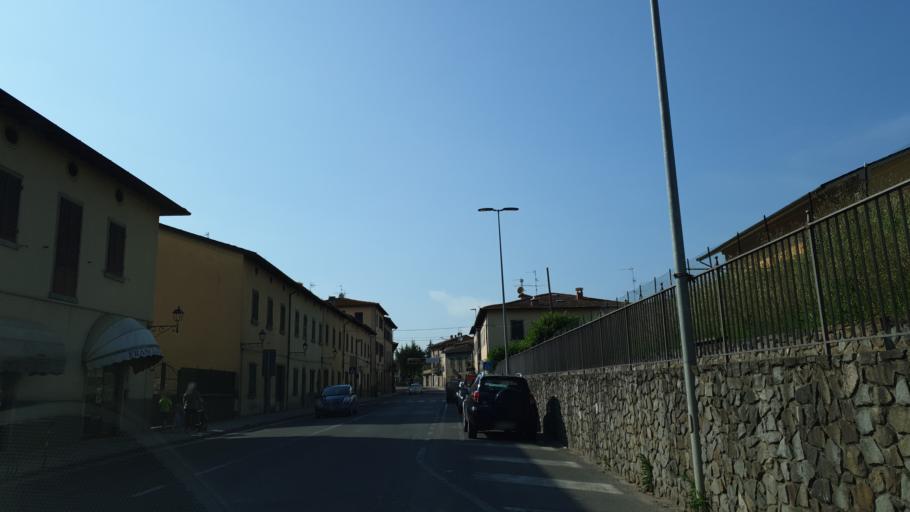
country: IT
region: Tuscany
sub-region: Province of Arezzo
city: Ponte a Poppi
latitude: 43.7305
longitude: 11.7675
